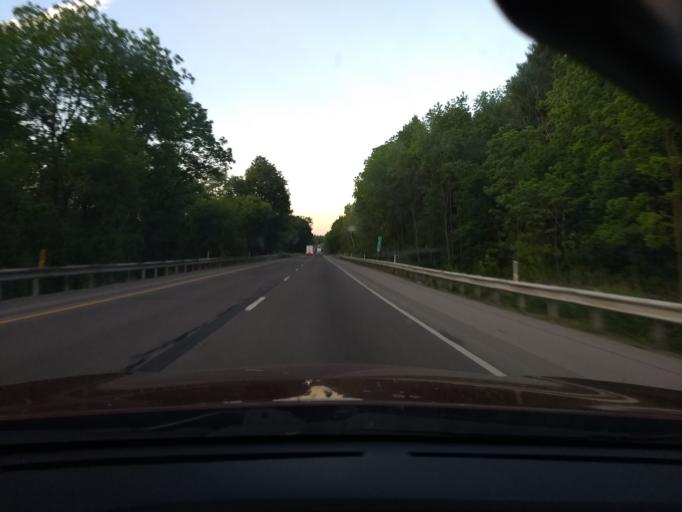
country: US
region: Pennsylvania
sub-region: Centre County
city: Zion
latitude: 40.9490
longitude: -77.6996
